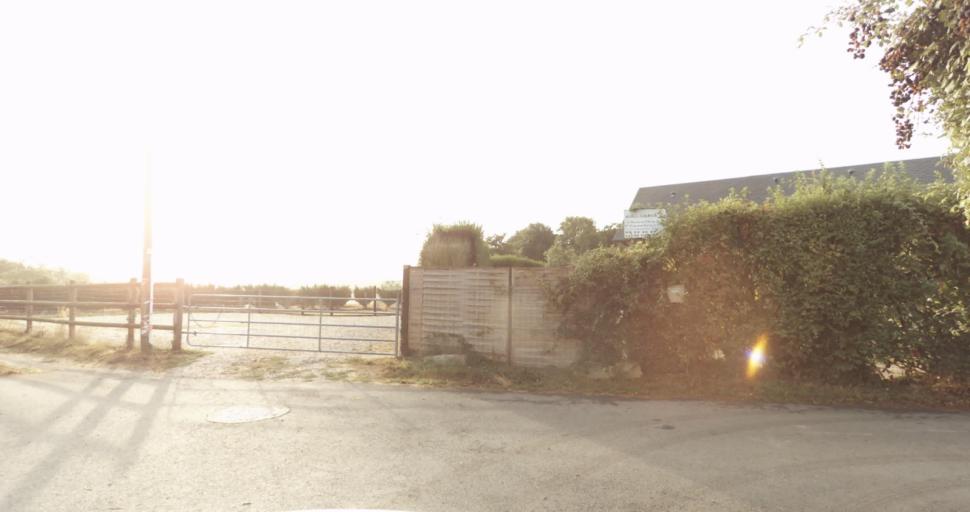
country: FR
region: Lower Normandy
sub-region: Departement de l'Orne
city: Vimoutiers
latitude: 48.9084
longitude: 0.2581
